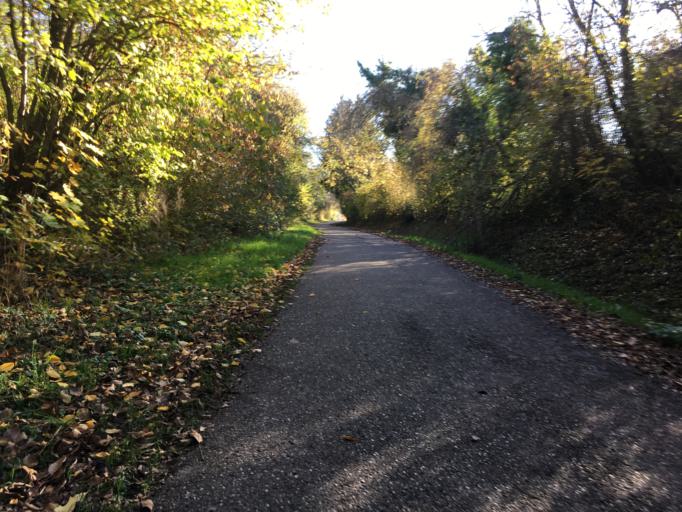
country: DE
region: Baden-Wuerttemberg
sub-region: Karlsruhe Region
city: Oberderdingen
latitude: 49.0568
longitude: 8.8042
